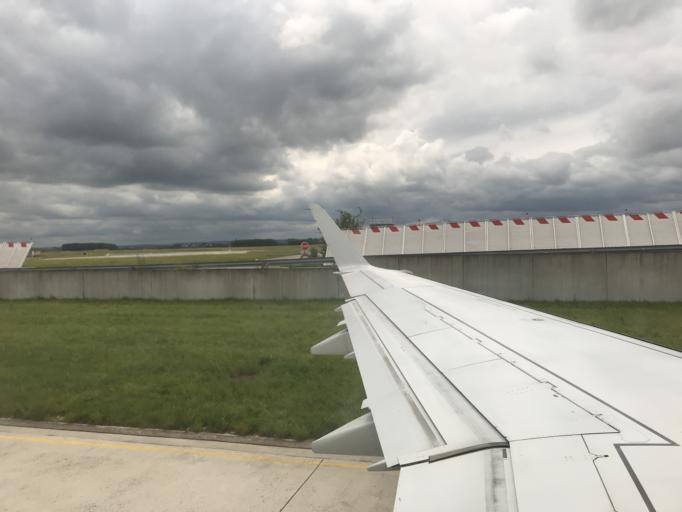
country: FR
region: Ile-de-France
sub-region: Departement de Seine-et-Marne
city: Mitry-Mory
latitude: 49.0031
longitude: 2.6024
